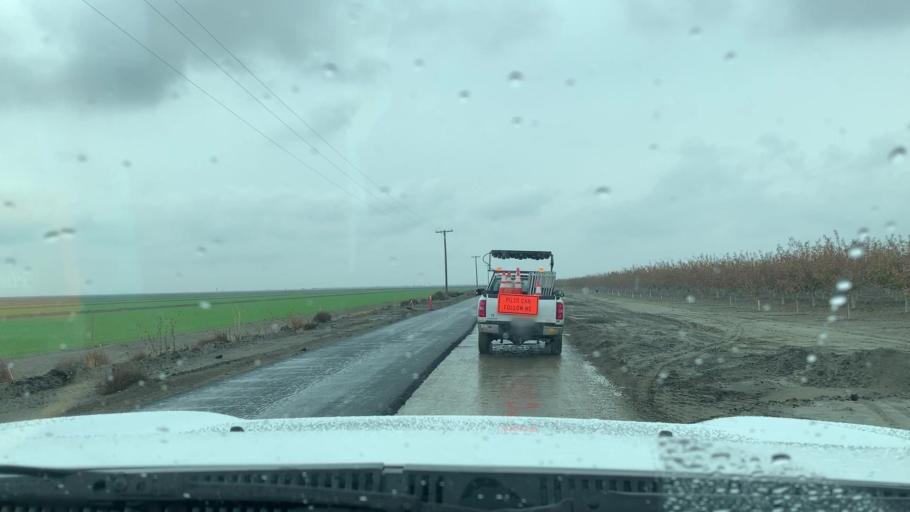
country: US
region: California
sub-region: Kings County
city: Corcoran
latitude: 36.0073
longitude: -119.5120
